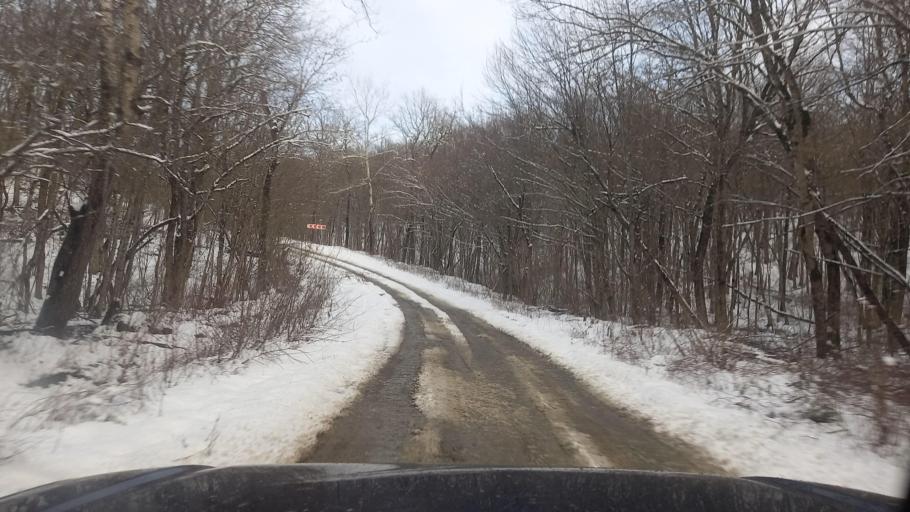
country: RU
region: Krasnodarskiy
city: Smolenskaya
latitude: 44.6749
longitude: 38.7623
